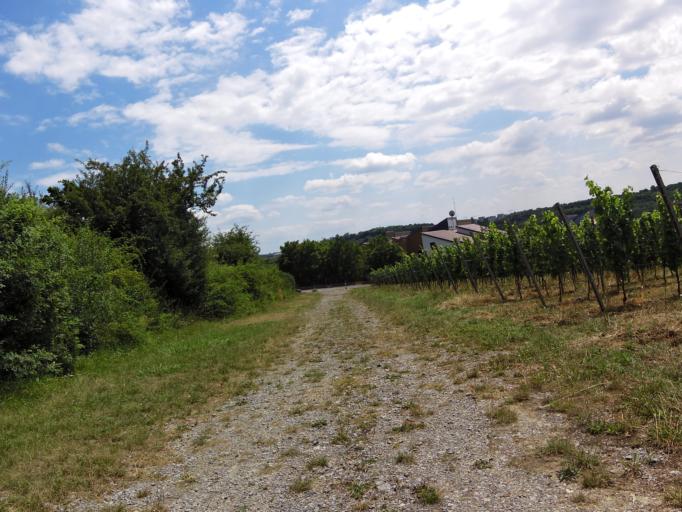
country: DE
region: Bavaria
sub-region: Regierungsbezirk Unterfranken
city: Wuerzburg
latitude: 49.8033
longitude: 9.9685
